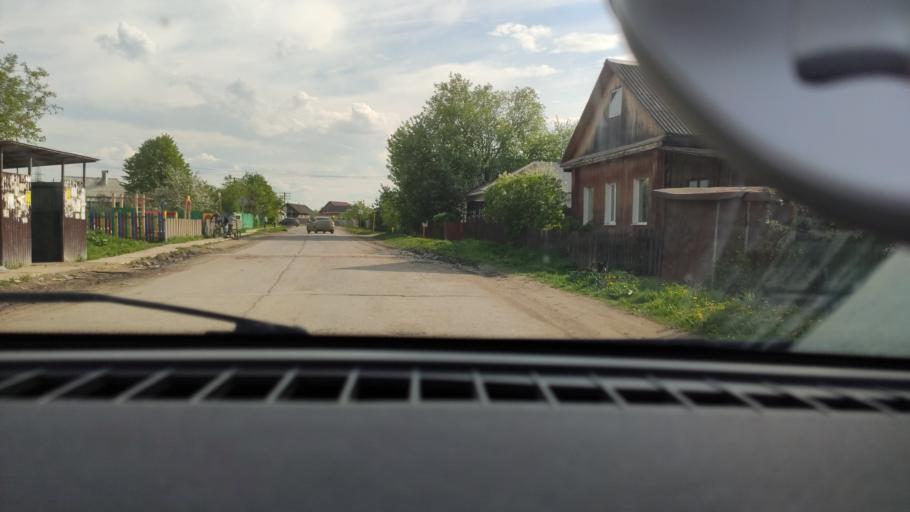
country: RU
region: Perm
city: Kultayevo
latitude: 57.9258
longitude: 56.0102
